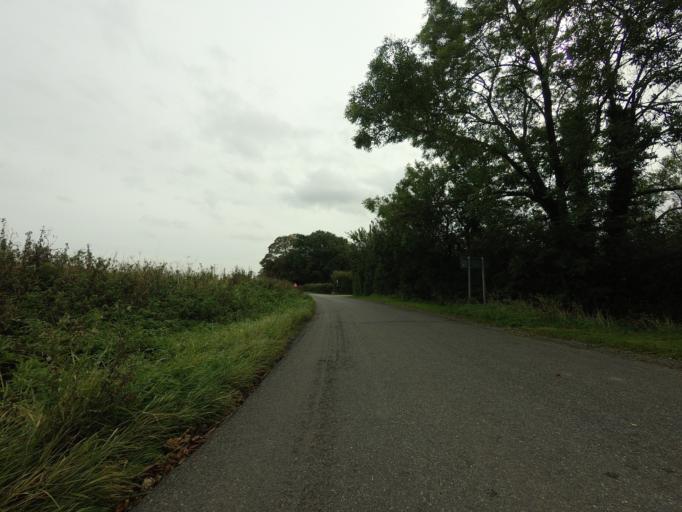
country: GB
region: England
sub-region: Hertfordshire
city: Buntingford
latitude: 51.9774
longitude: 0.0569
